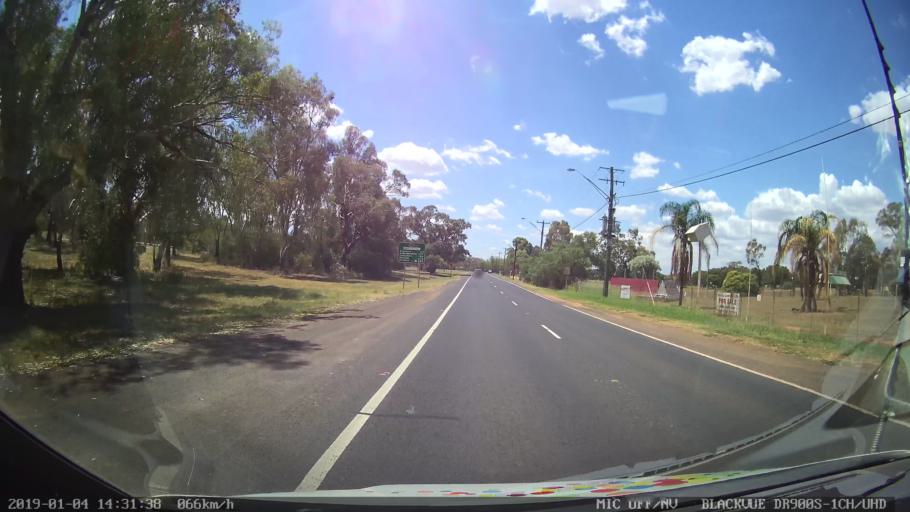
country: AU
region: New South Wales
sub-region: Dubbo Municipality
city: Dubbo
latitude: -32.2299
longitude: 148.6120
